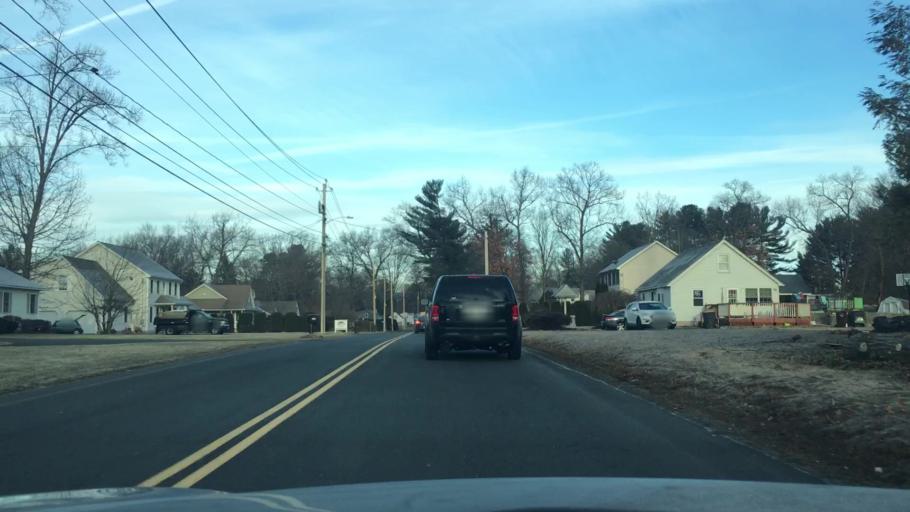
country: US
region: Massachusetts
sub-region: Hampden County
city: Westfield
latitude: 42.1335
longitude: -72.7236
